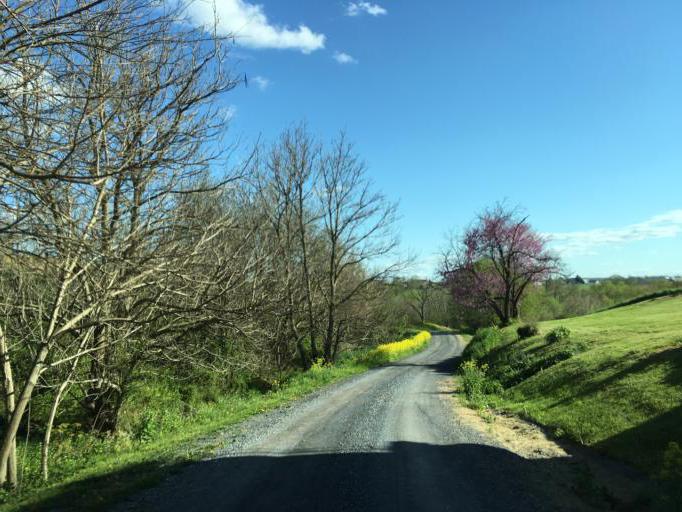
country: US
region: Maryland
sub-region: Carroll County
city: Taneytown
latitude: 39.6150
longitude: -77.2550
